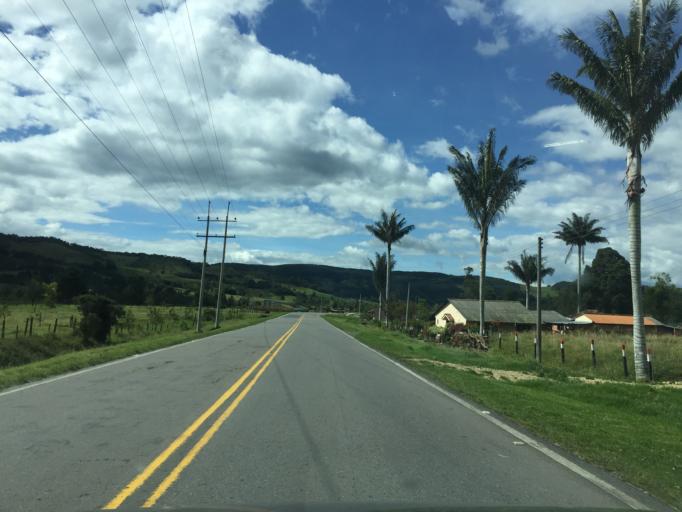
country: CO
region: Boyaca
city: Arcabuco
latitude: 5.7740
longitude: -73.4578
